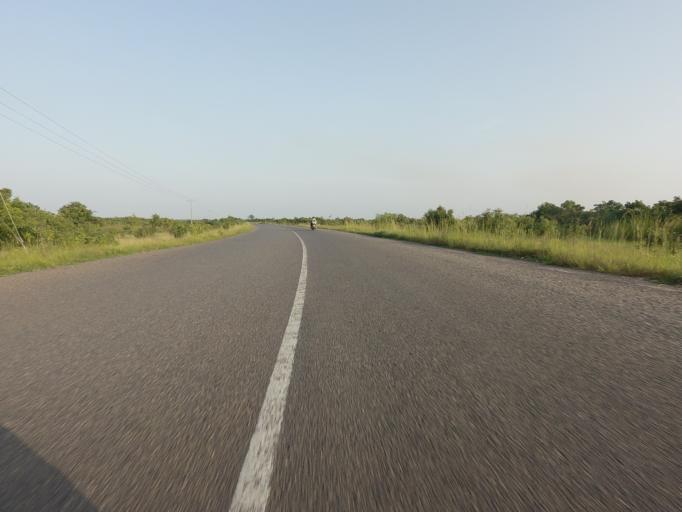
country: GH
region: Volta
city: Anloga
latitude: 5.9668
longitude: 0.6621
